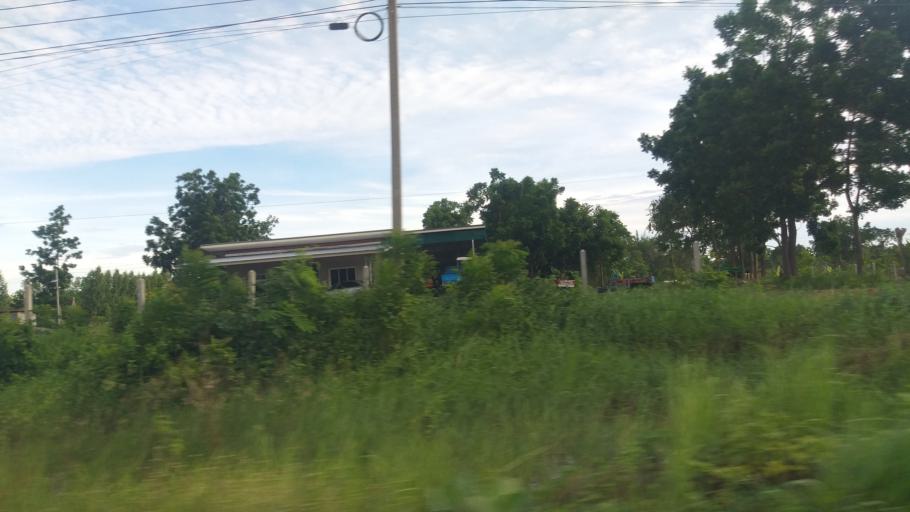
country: TH
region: Chaiyaphum
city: Phu Khiao
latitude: 16.3235
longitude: 102.2068
